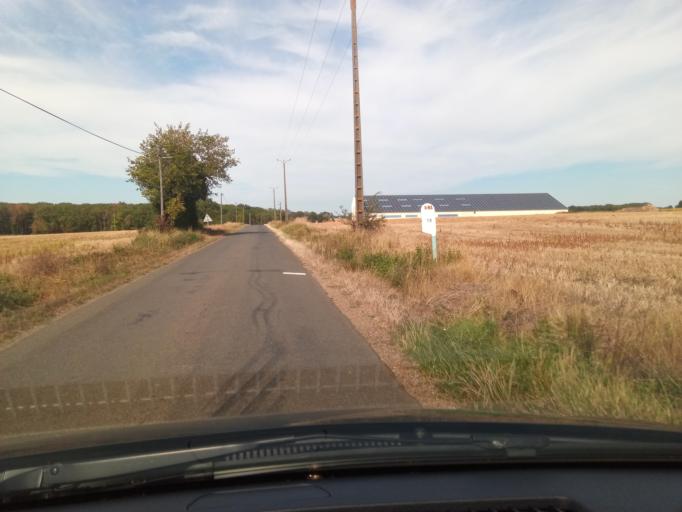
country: FR
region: Poitou-Charentes
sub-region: Departement de la Vienne
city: Chauvigny
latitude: 46.5393
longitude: 0.7395
